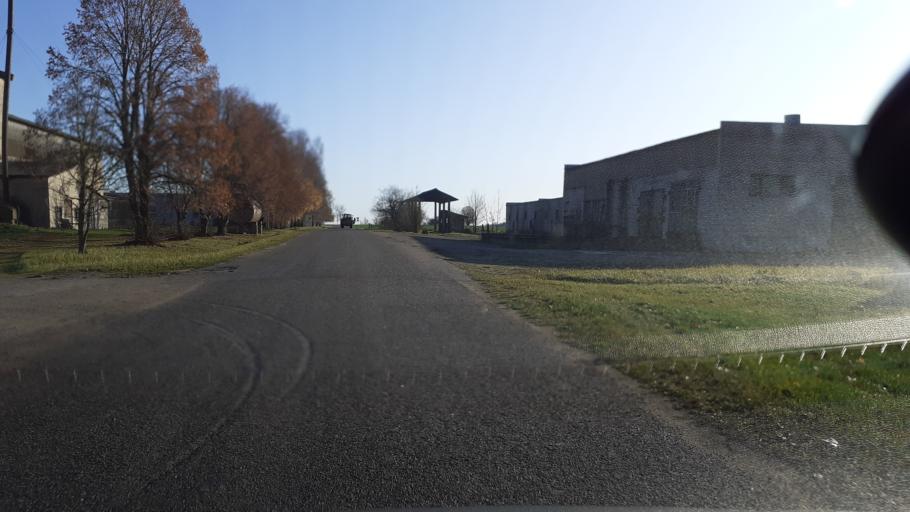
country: LV
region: Kuldigas Rajons
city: Kuldiga
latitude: 56.9972
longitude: 21.8961
